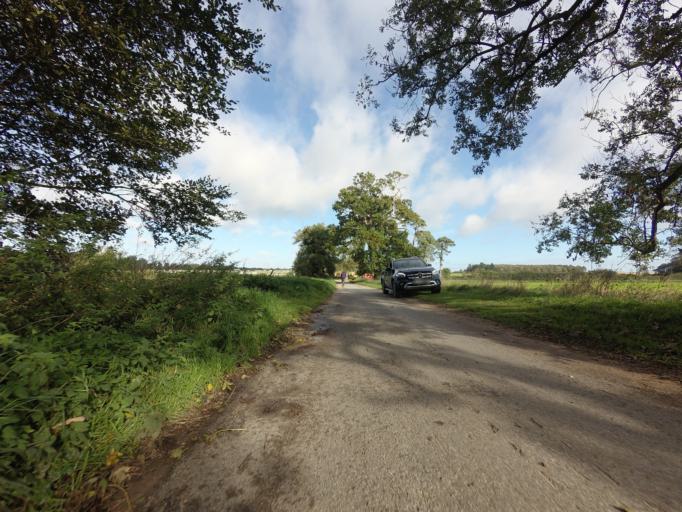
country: GB
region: England
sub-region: Norfolk
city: Dersingham
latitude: 52.8613
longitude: 0.6659
